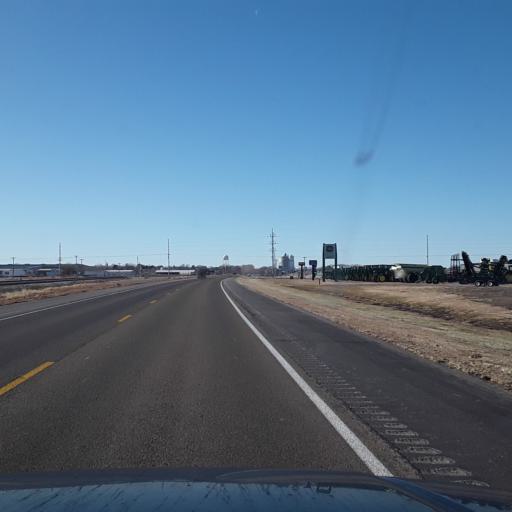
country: US
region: Nebraska
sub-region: Kearney County
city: Minden
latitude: 40.5090
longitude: -98.9289
